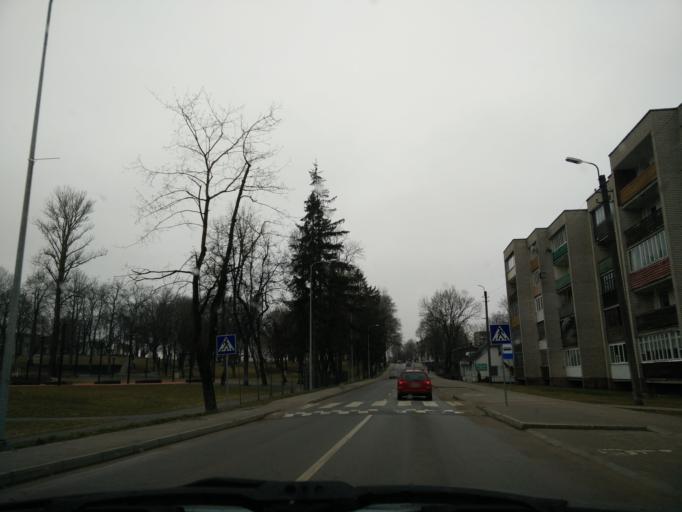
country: LT
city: Raseiniai
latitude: 55.3850
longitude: 23.1230
